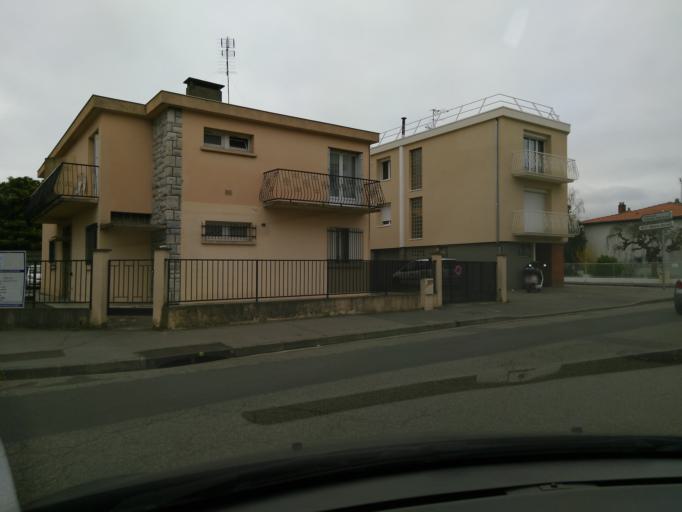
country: FR
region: Midi-Pyrenees
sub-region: Departement de la Haute-Garonne
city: Toulouse
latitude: 43.5786
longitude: 1.4616
